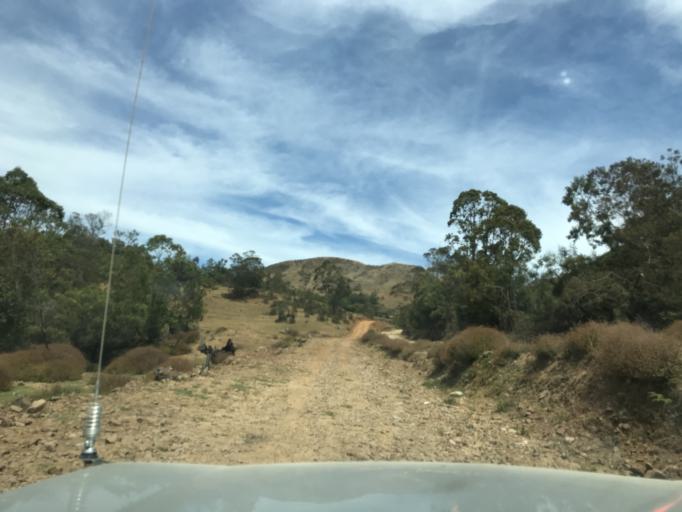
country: TL
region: Ainaro
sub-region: Ainaro
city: Ainaro
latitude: -8.8751
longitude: 125.5287
